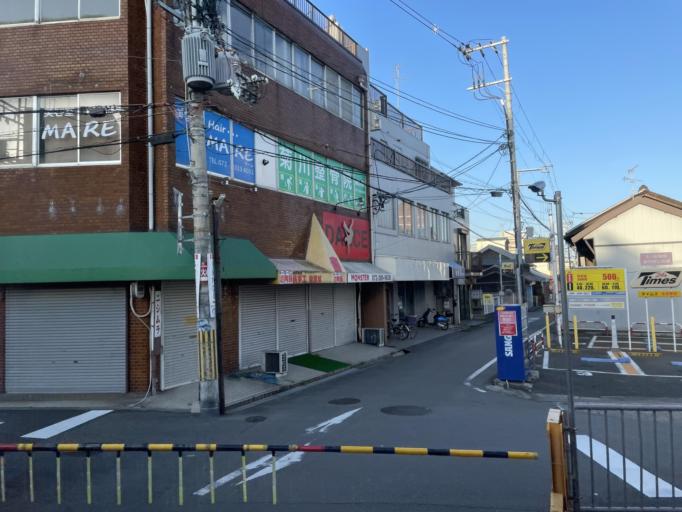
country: JP
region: Osaka
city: Matsubara
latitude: 34.5769
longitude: 135.5398
